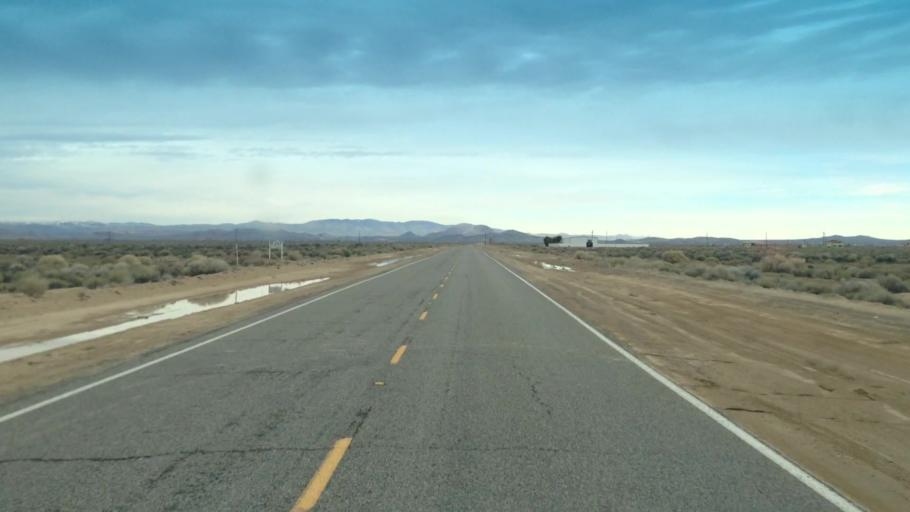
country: US
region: California
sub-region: Los Angeles County
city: Lancaster
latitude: 34.7413
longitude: -118.1842
